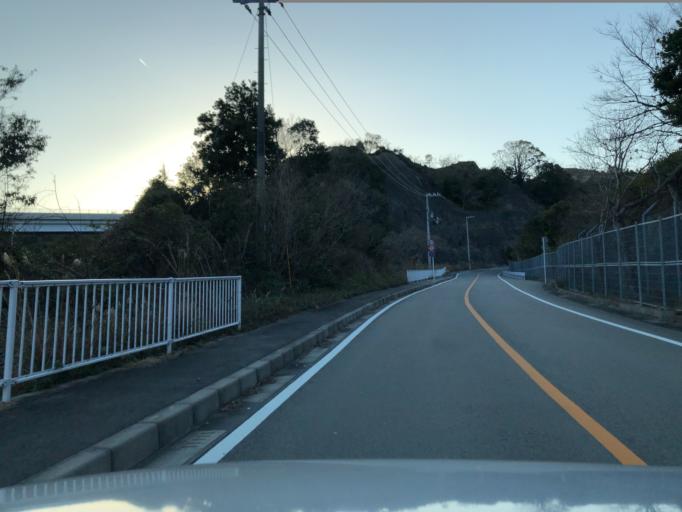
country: JP
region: Wakayama
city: Tanabe
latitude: 33.6630
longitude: 135.3702
